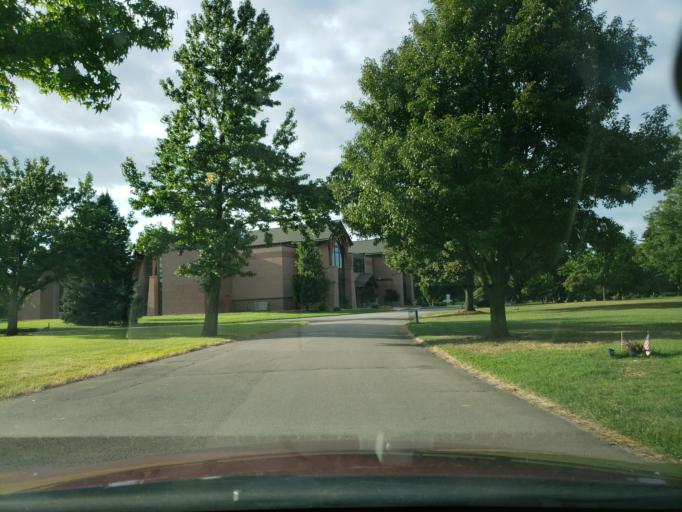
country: US
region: New York
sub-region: Monroe County
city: Irondequoit
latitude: 43.2106
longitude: -77.6309
